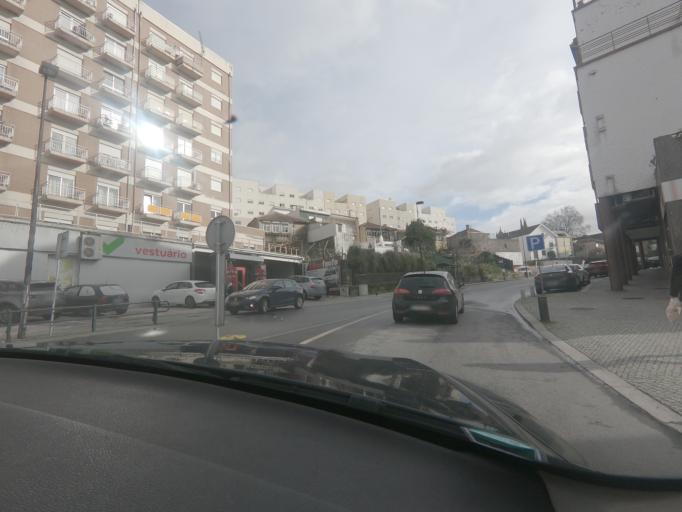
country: PT
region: Vila Real
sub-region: Vila Real
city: Vila Real
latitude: 41.2975
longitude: -7.7489
